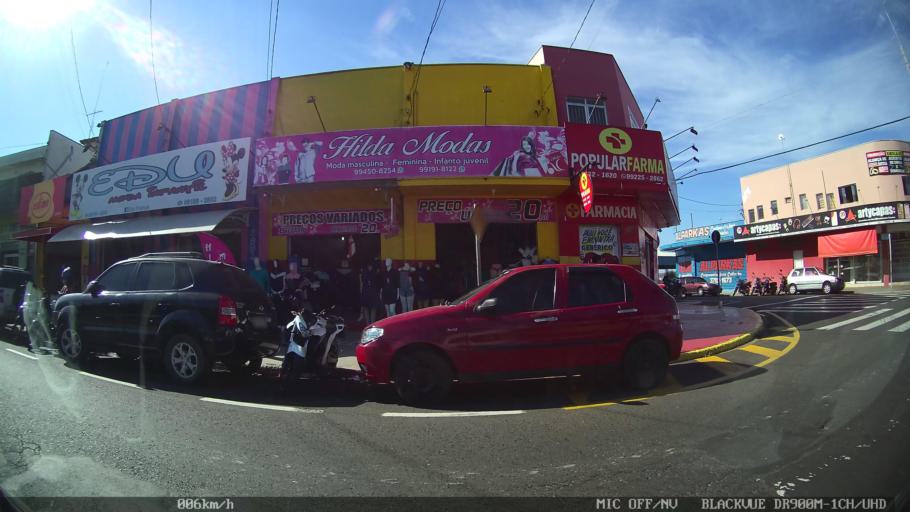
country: BR
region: Sao Paulo
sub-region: Franca
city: Franca
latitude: -20.5034
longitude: -47.4067
